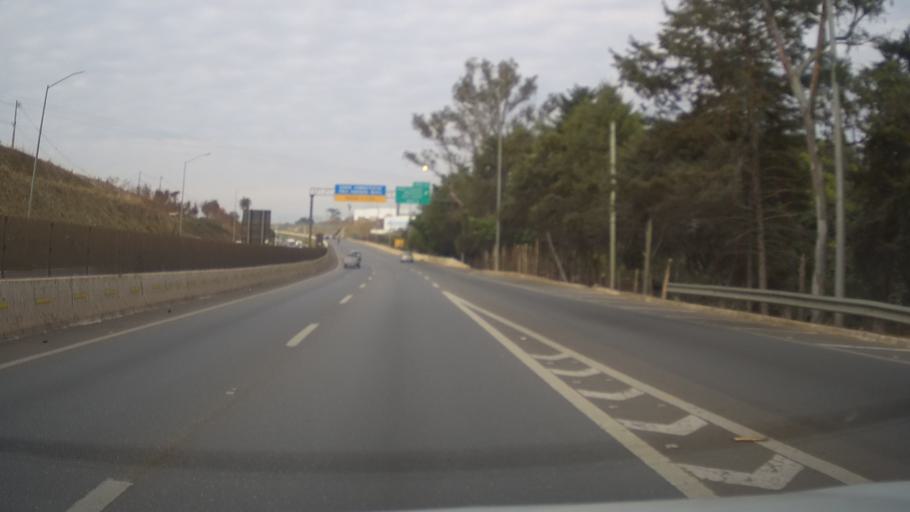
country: BR
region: Minas Gerais
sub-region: Vespasiano
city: Vespasiano
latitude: -19.7304
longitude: -43.9417
